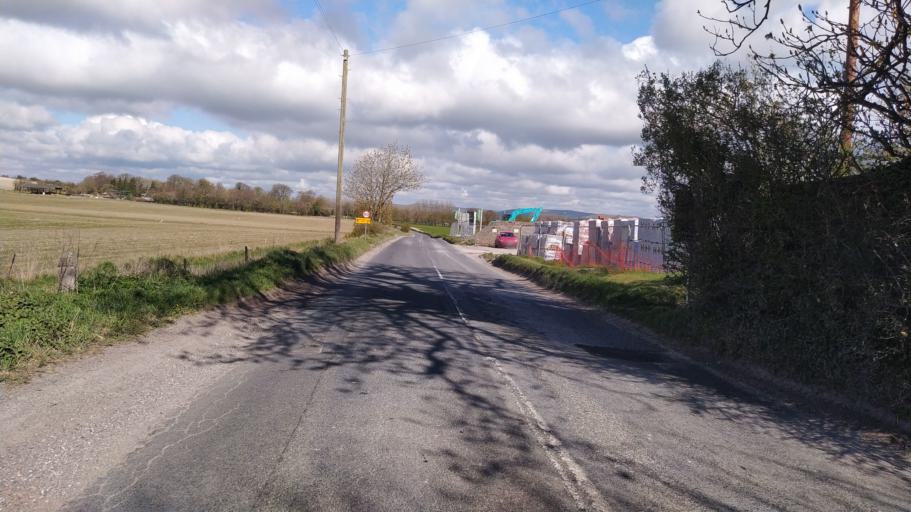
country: GB
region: England
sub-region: Wiltshire
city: Rushall
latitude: 51.2937
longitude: -1.8155
